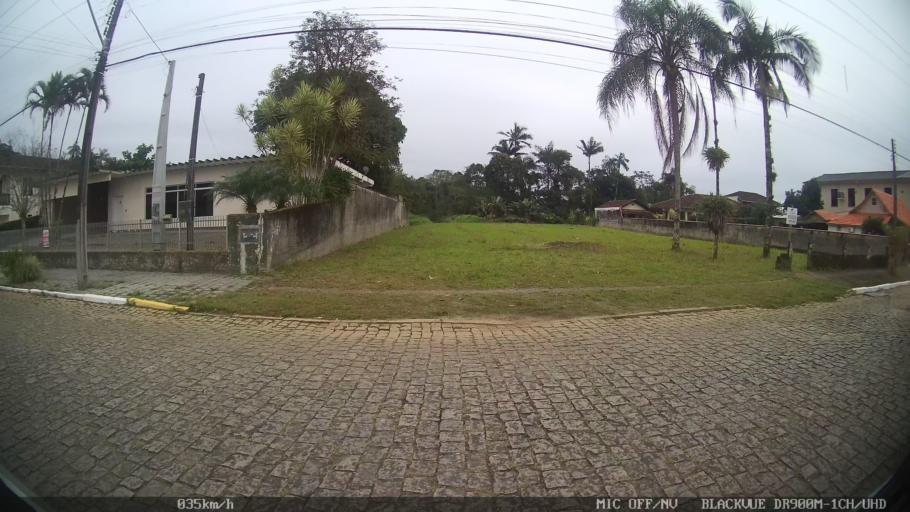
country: BR
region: Santa Catarina
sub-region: Joinville
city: Joinville
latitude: -26.2074
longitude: -48.9118
